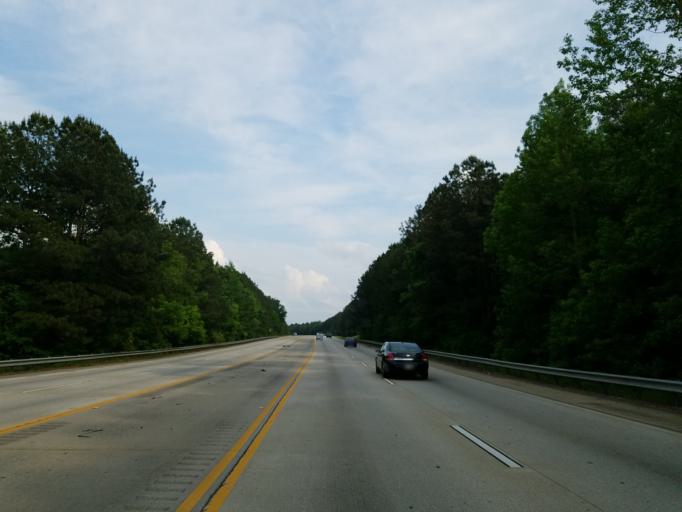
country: US
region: Georgia
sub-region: Cobb County
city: Powder Springs
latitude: 33.8356
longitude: -84.6795
